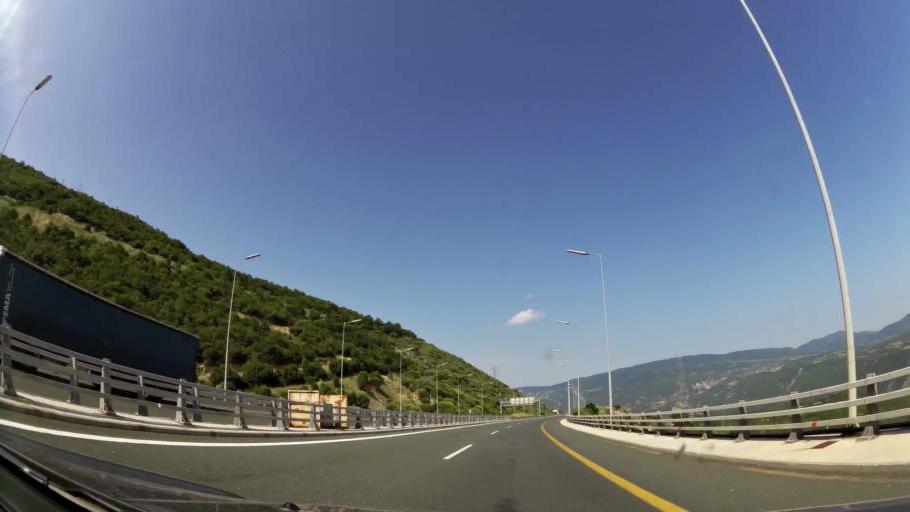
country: GR
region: Central Macedonia
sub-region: Nomos Imathias
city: Rizomata
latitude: 40.3886
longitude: 22.1480
